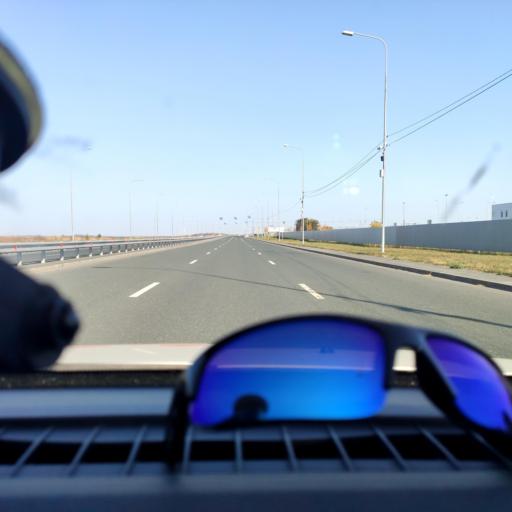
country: RU
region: Samara
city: Bereza
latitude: 53.5133
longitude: 50.1484
